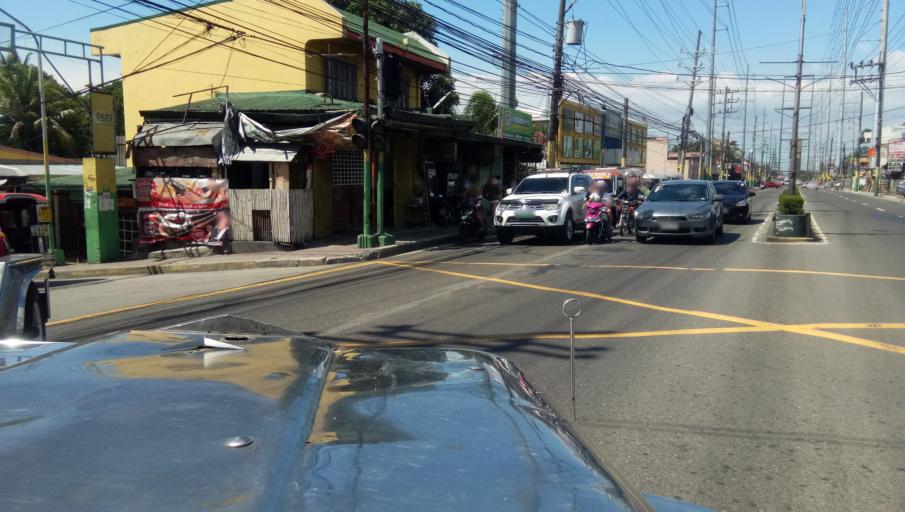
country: PH
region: Calabarzon
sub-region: Province of Cavite
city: Dasmarinas
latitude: 14.3317
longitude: 120.9390
